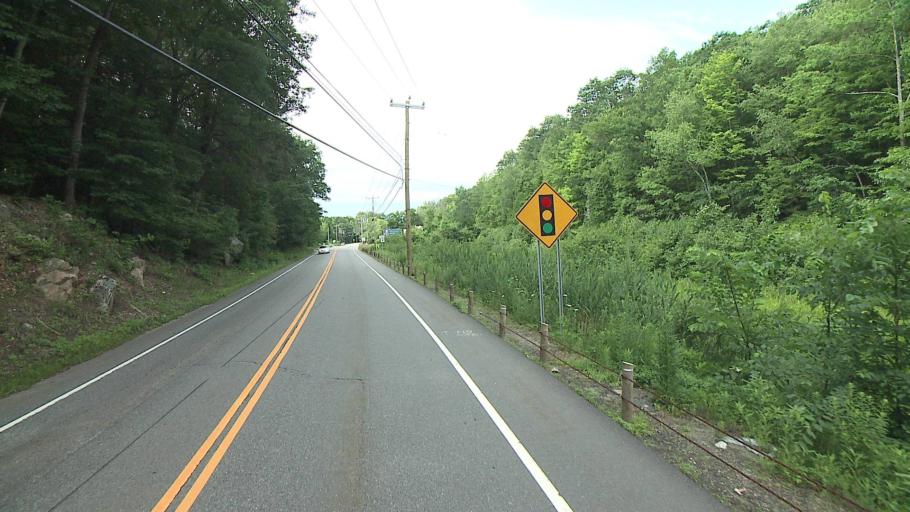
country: US
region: Connecticut
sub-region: Litchfield County
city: Torrington
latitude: 41.8335
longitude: -73.1045
